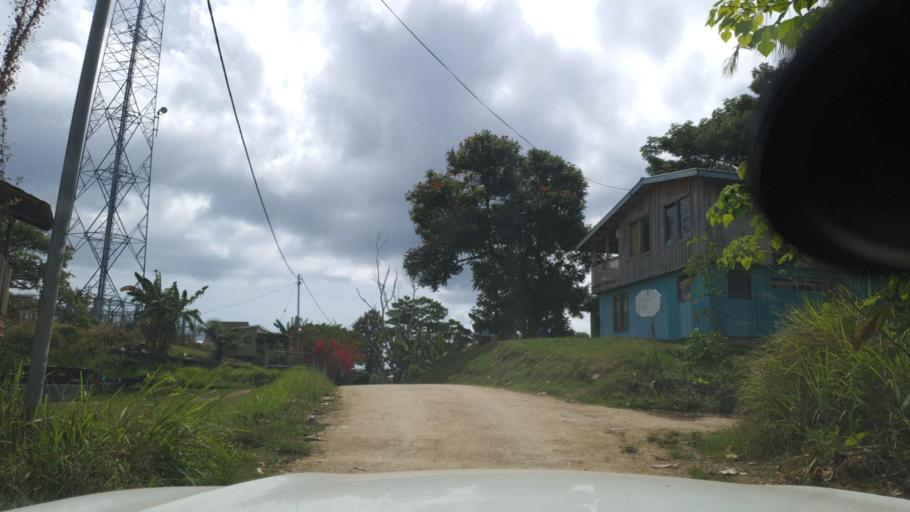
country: SB
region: Guadalcanal
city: Honiara
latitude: -9.4296
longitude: 159.9299
